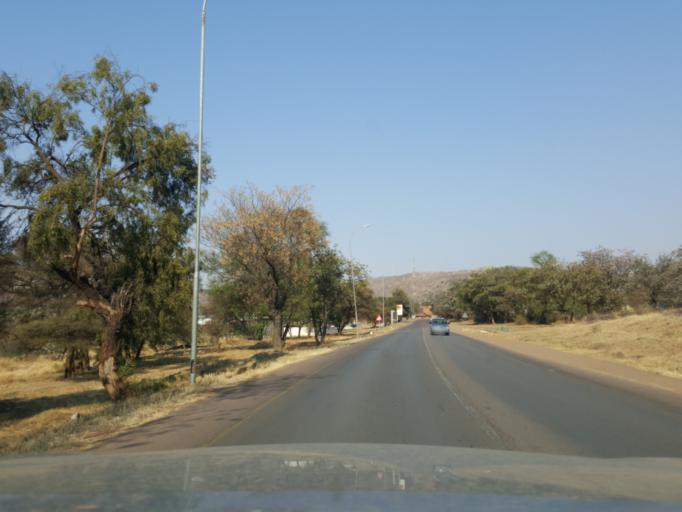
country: BW
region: South East
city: Lobatse
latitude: -25.2272
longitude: 25.6756
